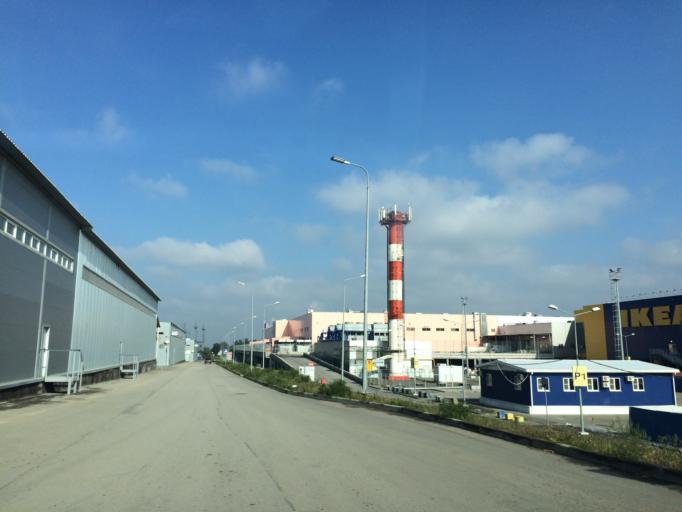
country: RU
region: Rostov
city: Aksay
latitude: 47.2874
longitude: 39.8442
